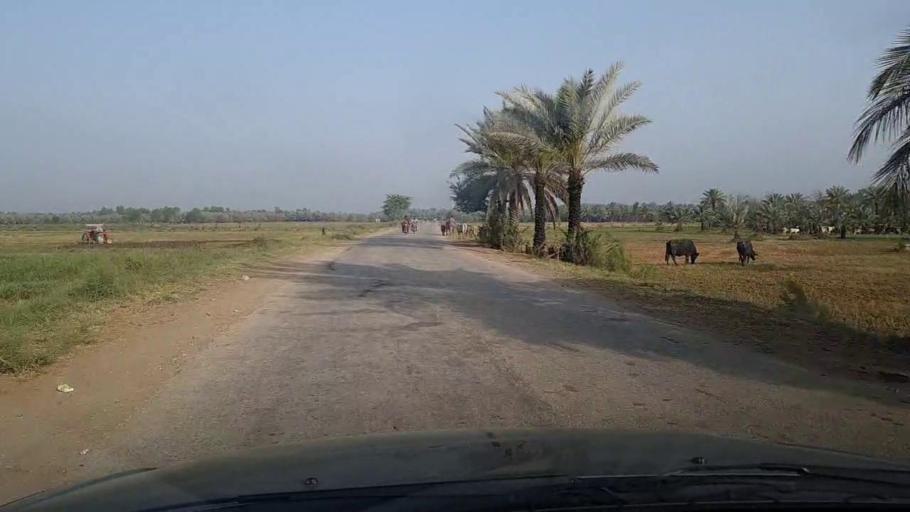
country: PK
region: Sindh
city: Khairpur
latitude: 27.5509
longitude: 68.6904
